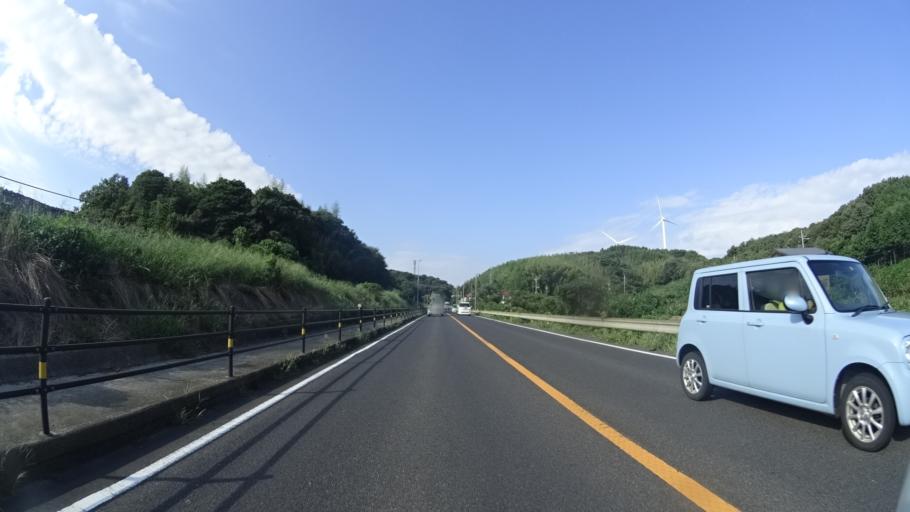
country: JP
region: Shimane
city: Izumo
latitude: 35.2933
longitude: 132.6409
